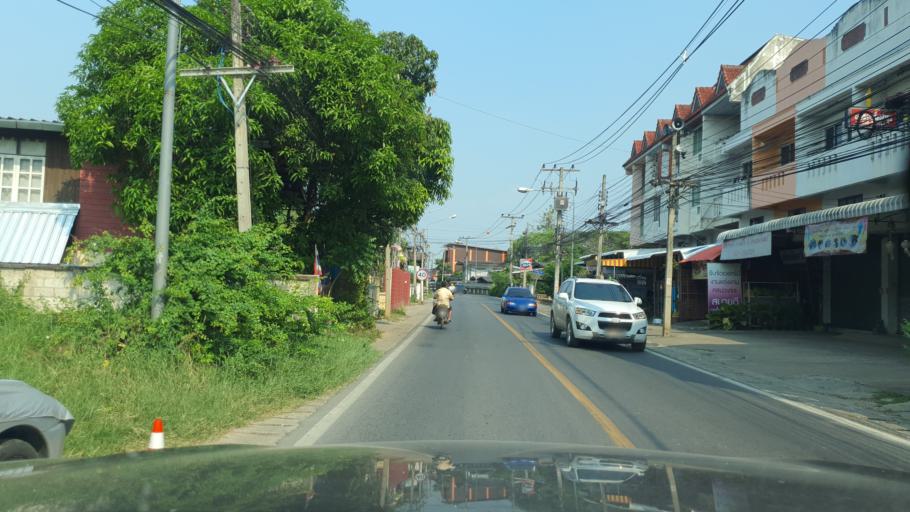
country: TH
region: Lamphun
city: Lamphun
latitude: 18.5812
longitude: 98.9974
